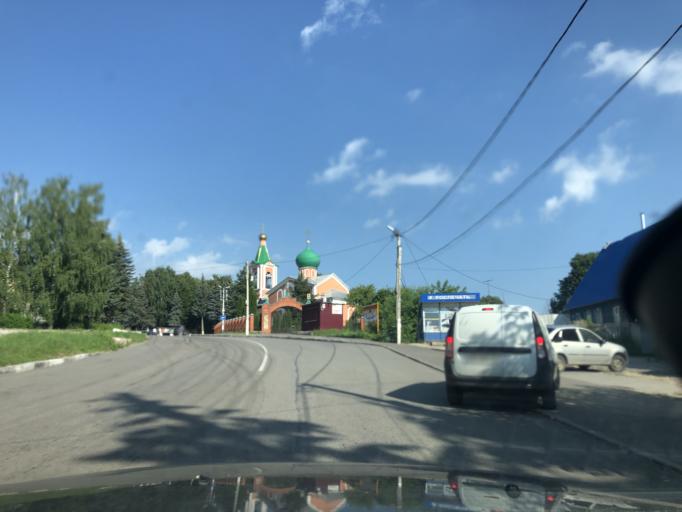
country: RU
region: Tula
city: Dubna
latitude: 54.1520
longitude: 36.9611
